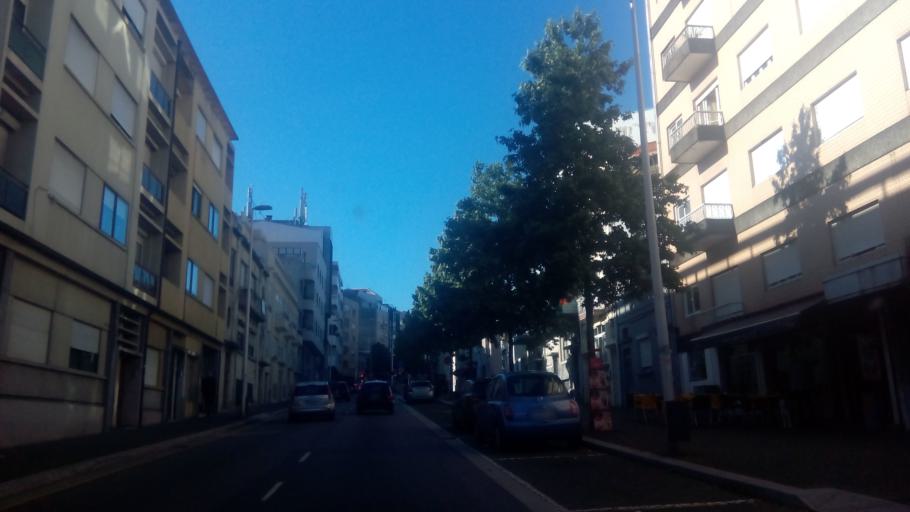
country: PT
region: Porto
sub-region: Porto
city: Porto
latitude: 41.1560
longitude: -8.6092
